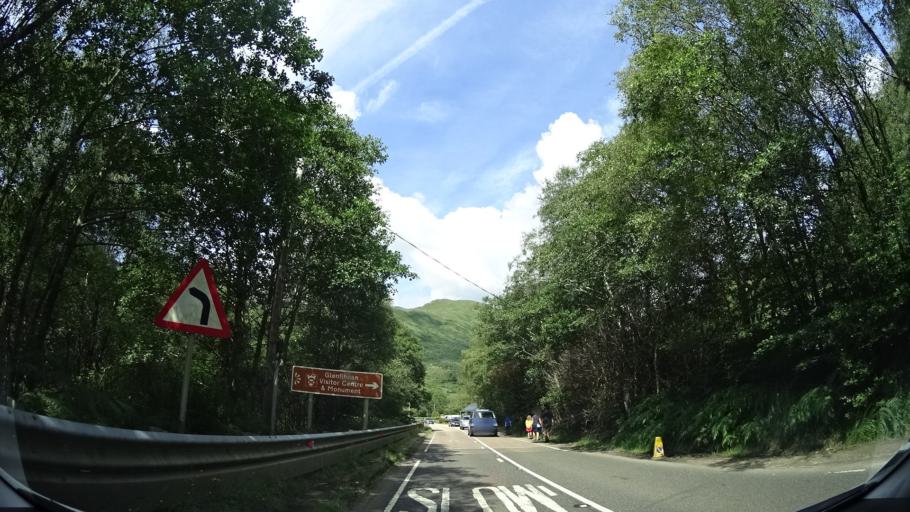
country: GB
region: Scotland
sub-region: Highland
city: Fort William
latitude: 56.8692
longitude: -5.4346
